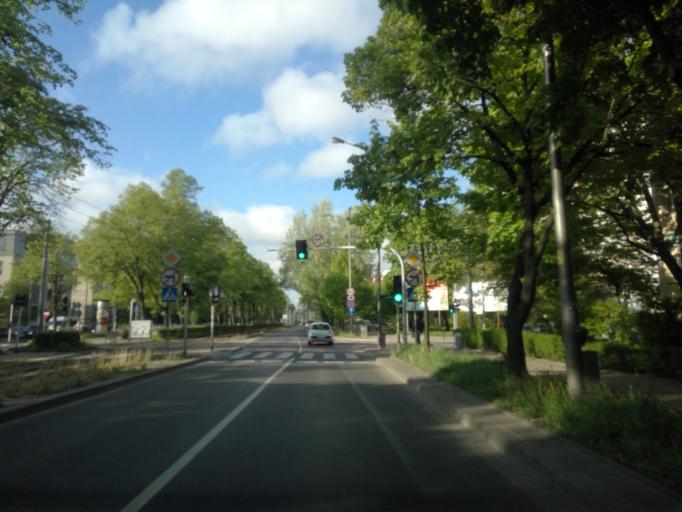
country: PL
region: Lower Silesian Voivodeship
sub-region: Powiat wroclawski
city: Wroclaw
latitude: 51.0827
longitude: 17.0093
